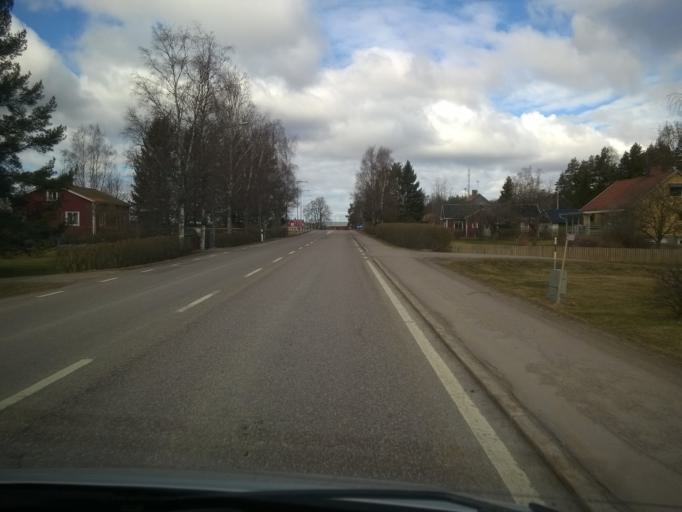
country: SE
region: Uppsala
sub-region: Tierps Kommun
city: Tierp
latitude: 60.2192
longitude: 17.4722
